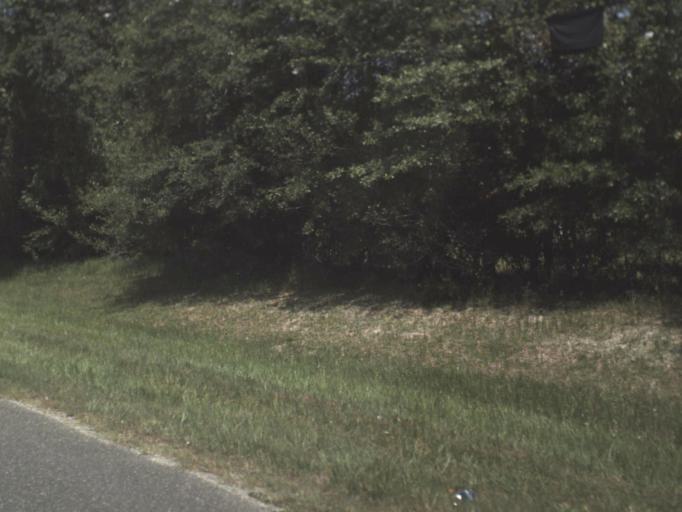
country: US
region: Florida
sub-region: Columbia County
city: Lake City
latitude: 30.1382
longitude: -82.7081
